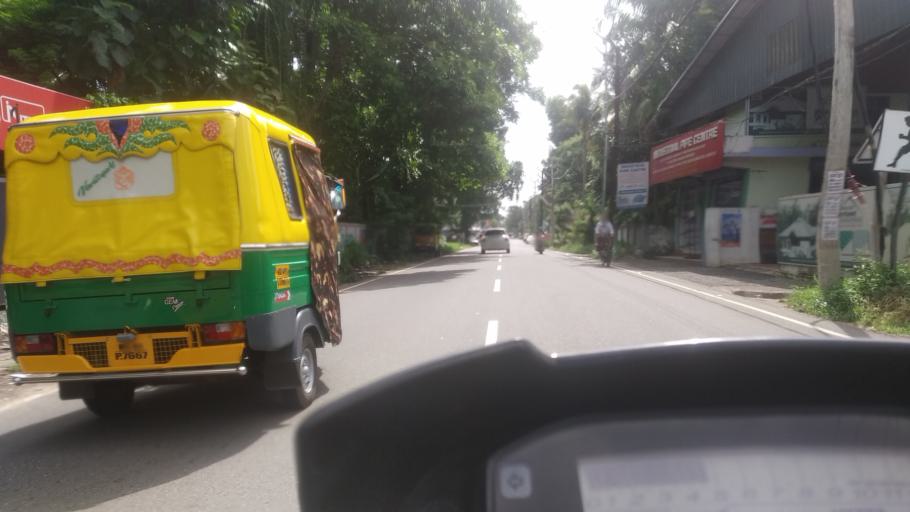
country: IN
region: Kerala
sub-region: Ernakulam
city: Elur
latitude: 10.1459
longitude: 76.2563
